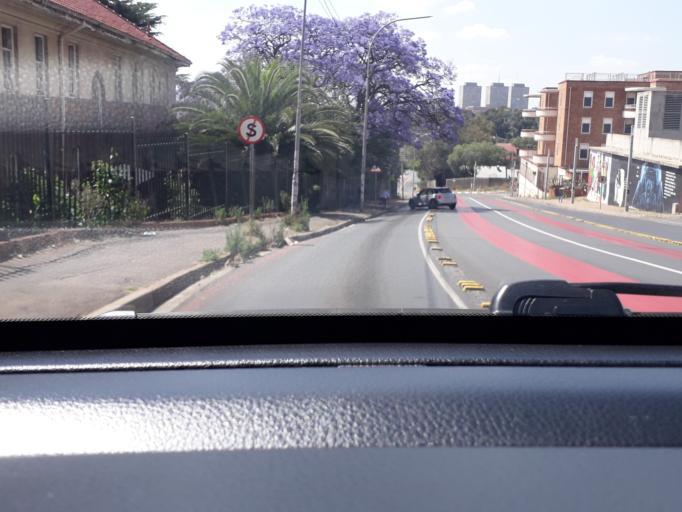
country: ZA
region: Gauteng
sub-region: City of Johannesburg Metropolitan Municipality
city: Johannesburg
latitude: -26.1883
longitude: 28.0410
